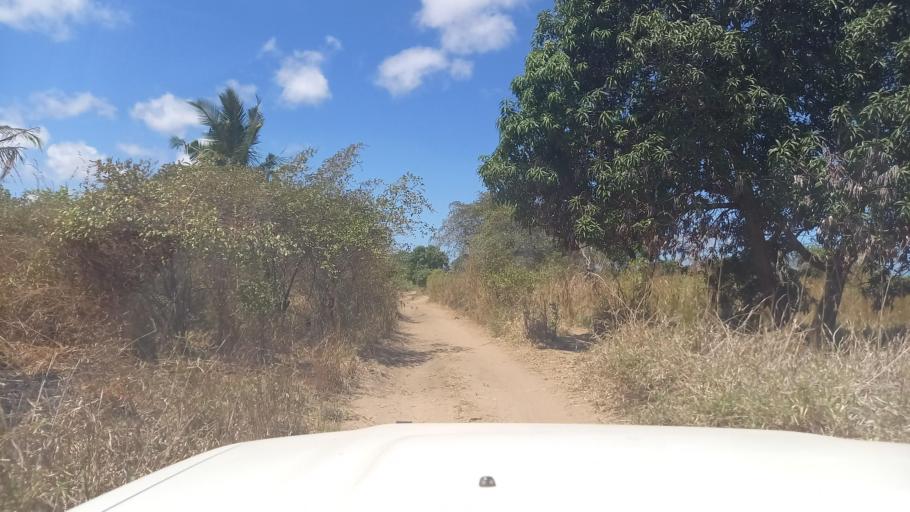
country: MZ
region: Cabo Delgado
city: Pemba
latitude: -13.4241
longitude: 40.4886
